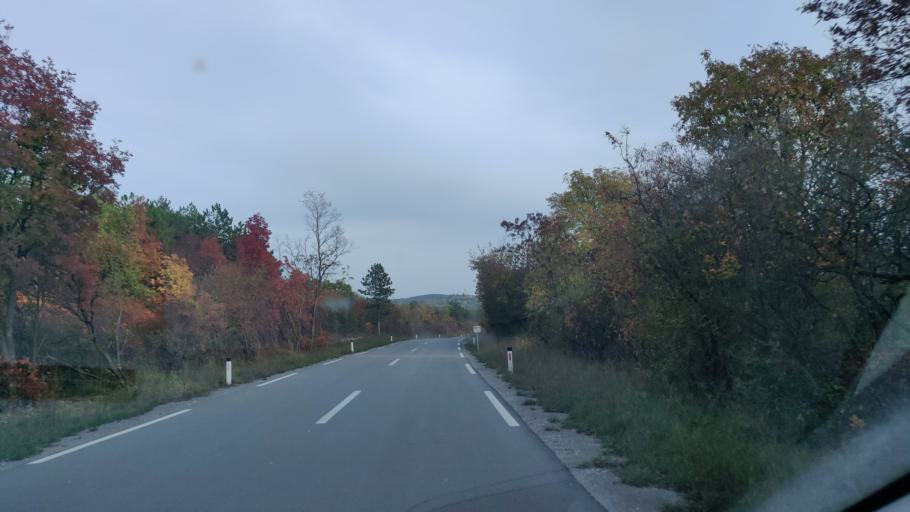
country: SI
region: Miren-Kostanjevica
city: Miren
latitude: 45.8491
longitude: 13.6126
